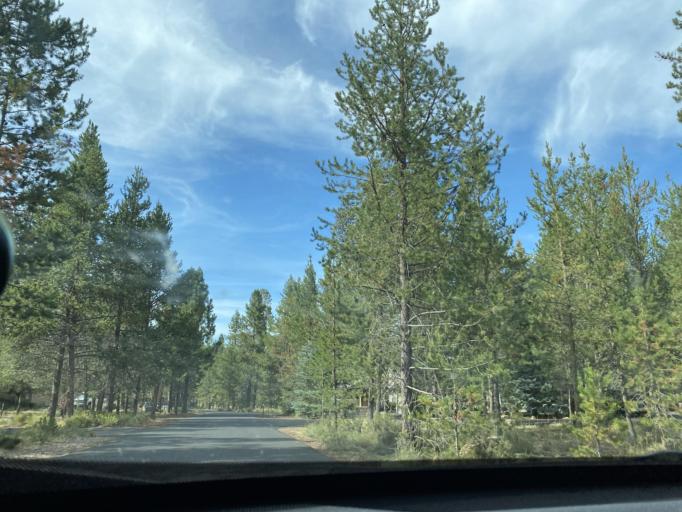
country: US
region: Oregon
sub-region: Deschutes County
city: Sunriver
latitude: 43.8964
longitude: -121.4399
